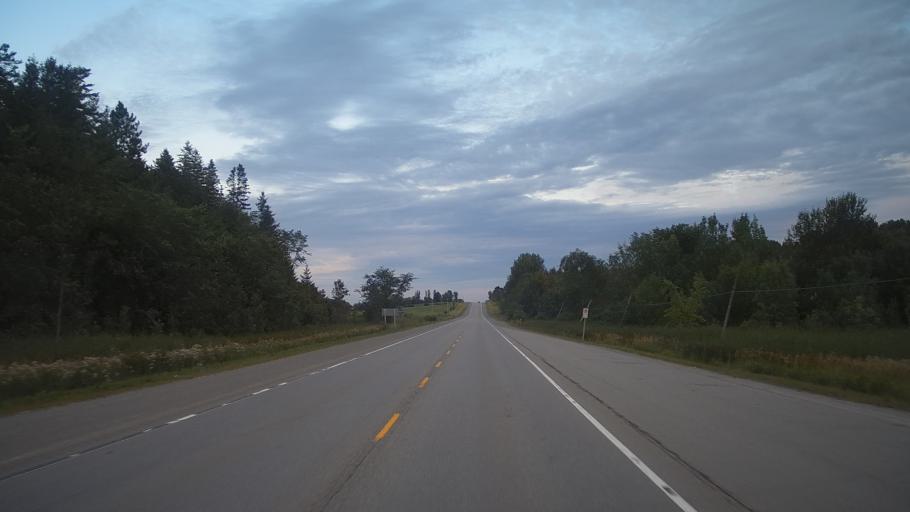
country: CA
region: Ontario
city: Pembroke
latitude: 45.7202
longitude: -76.9894
